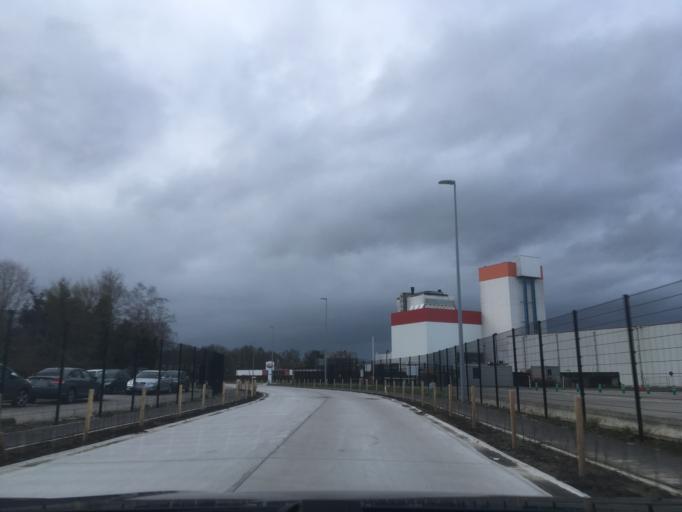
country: BE
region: Flanders
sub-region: Provincie West-Vlaanderen
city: Oostrozebeke
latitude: 50.9034
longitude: 3.3318
